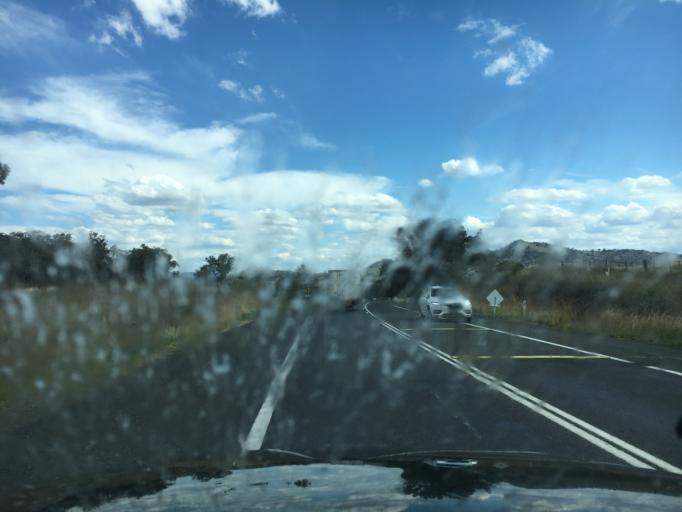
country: AU
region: New South Wales
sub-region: Liverpool Plains
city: Quirindi
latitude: -31.4657
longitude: 150.8611
